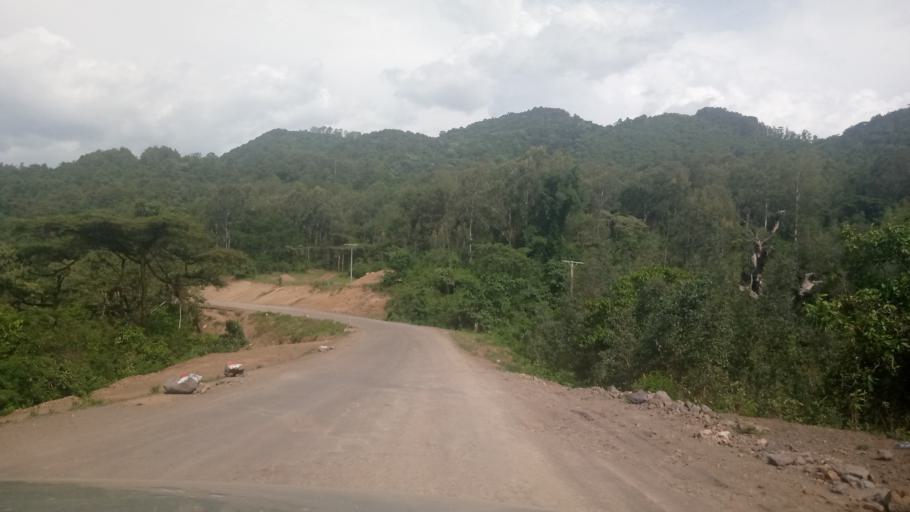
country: ET
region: Oromiya
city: Agaro
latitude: 8.0431
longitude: 36.4672
